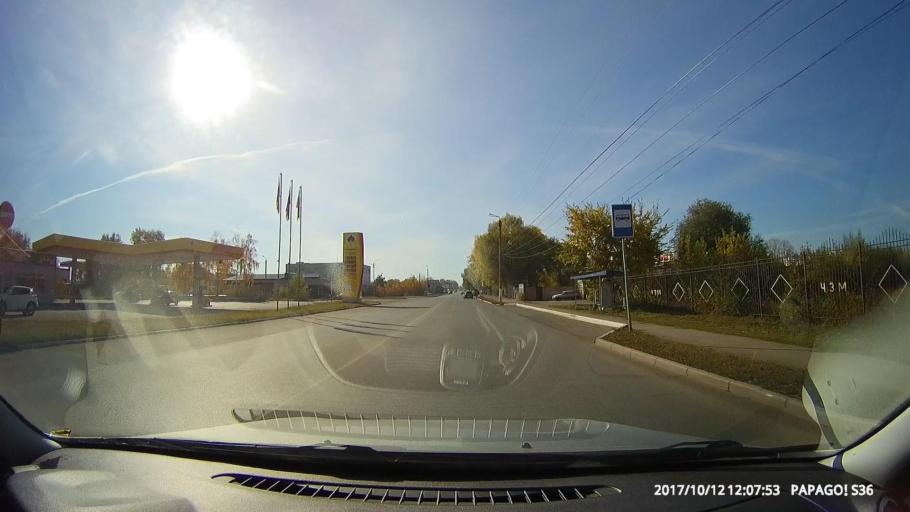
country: RU
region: Samara
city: Chapayevsk
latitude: 52.9649
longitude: 49.6990
